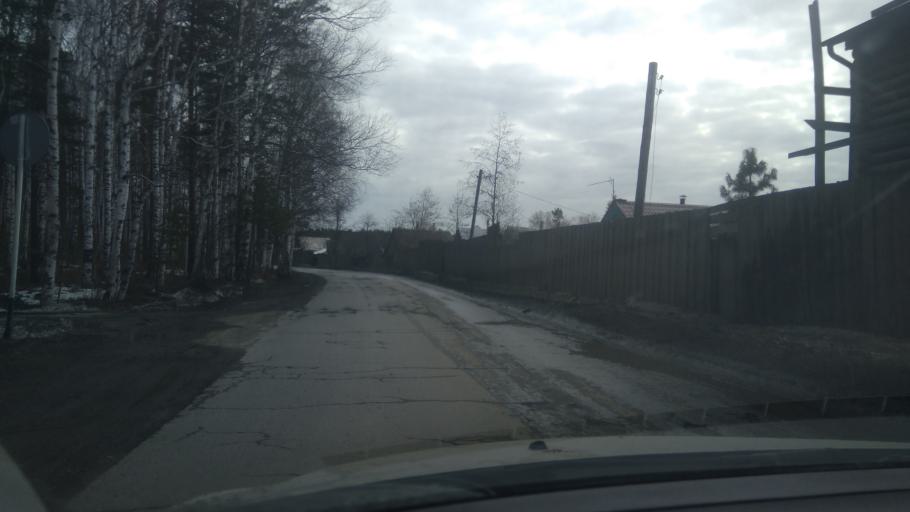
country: RU
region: Sverdlovsk
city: Severka
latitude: 56.8444
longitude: 60.3836
